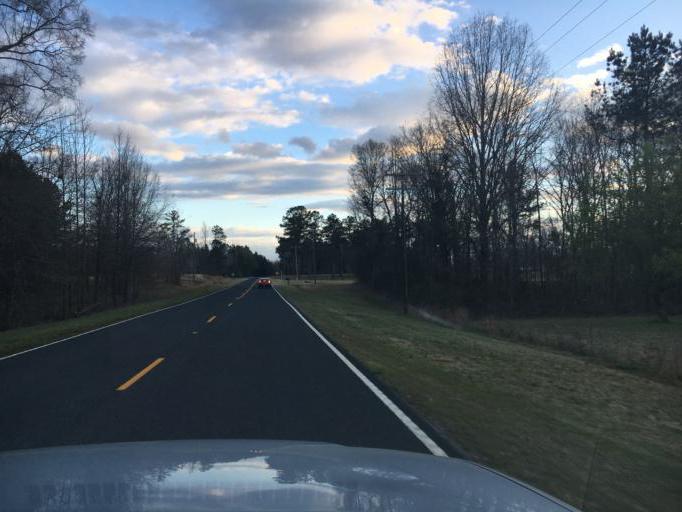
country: US
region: South Carolina
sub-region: Greenwood County
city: Greenwood
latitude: 34.1005
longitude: -82.1874
